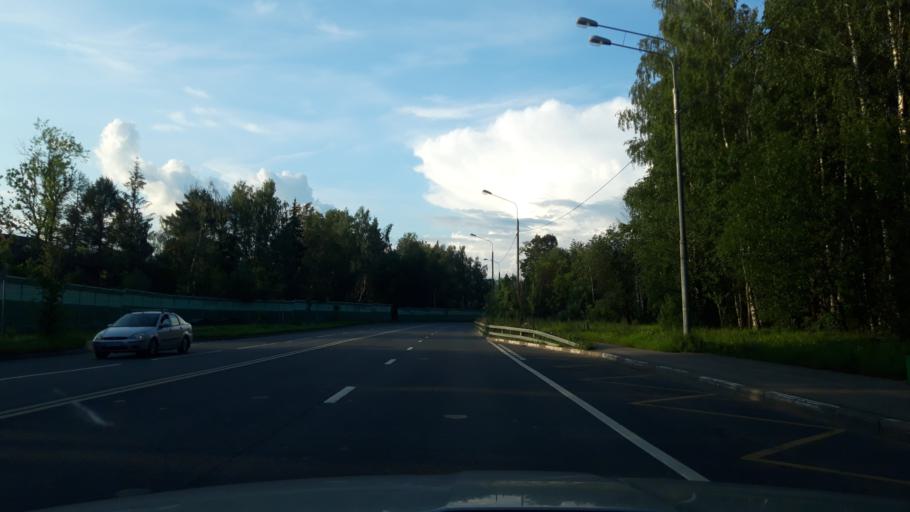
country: RU
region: Moskovskaya
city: Alabushevo
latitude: 56.0016
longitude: 37.1633
